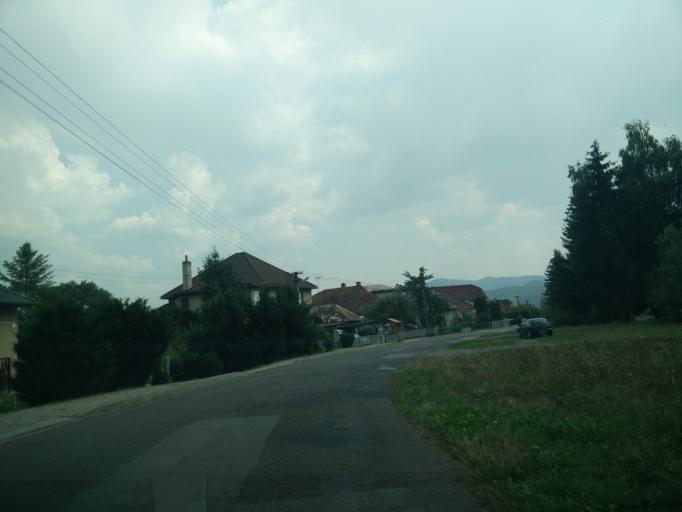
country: SK
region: Banskobystricky
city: Zarnovica
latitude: 48.5511
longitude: 18.7591
